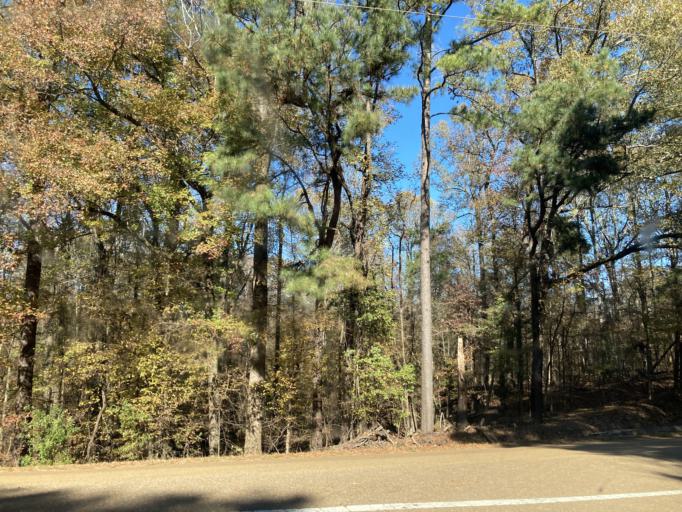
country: US
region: Mississippi
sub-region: Hinds County
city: Lynchburg
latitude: 32.5960
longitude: -90.5372
